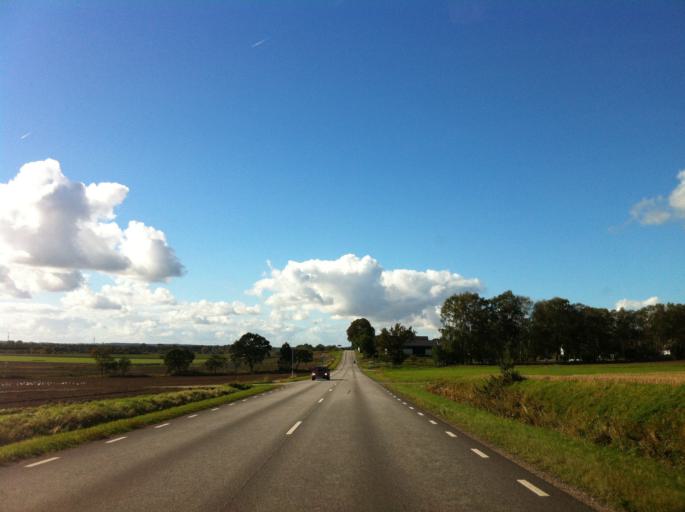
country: SE
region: Skane
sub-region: Hoors Kommun
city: Loberod
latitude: 55.7258
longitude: 13.4977
